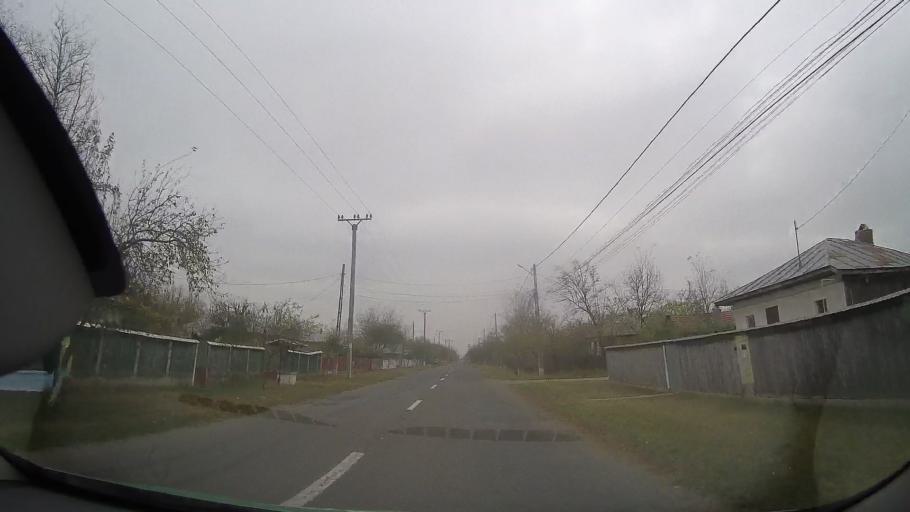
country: RO
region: Ialomita
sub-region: Comuna Grindu
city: Grindu
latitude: 44.7778
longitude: 26.9061
